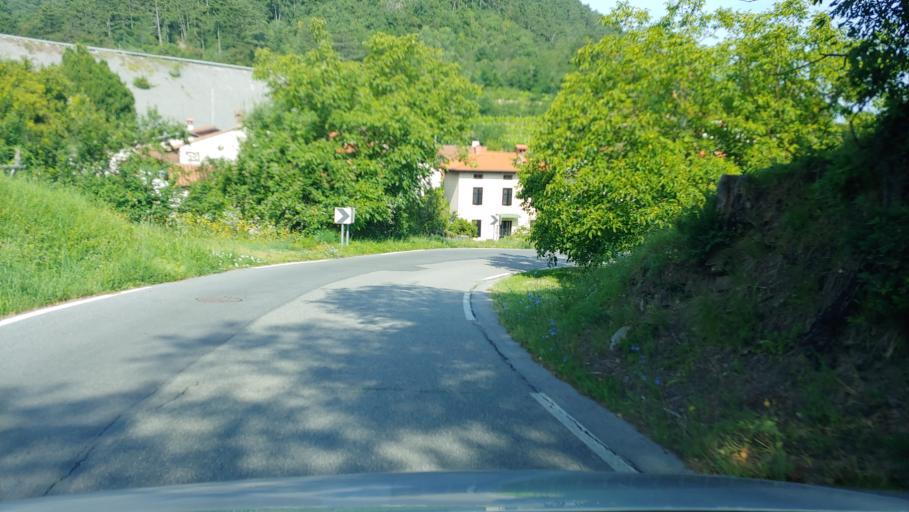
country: SI
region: Komen
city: Komen
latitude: 45.8540
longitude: 13.7889
